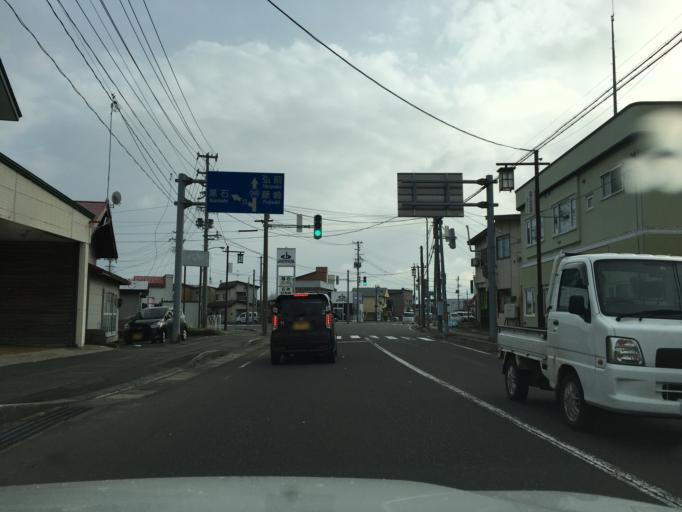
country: JP
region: Aomori
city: Namioka
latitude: 40.7114
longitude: 140.5899
